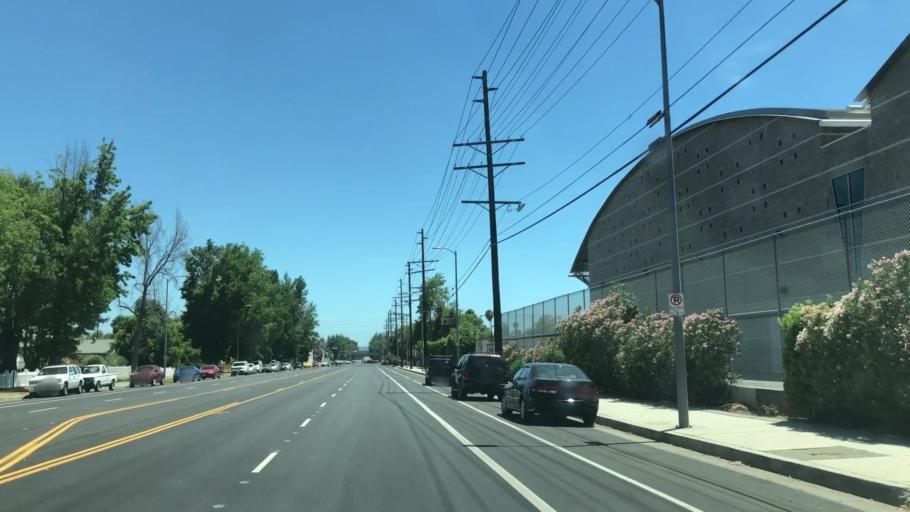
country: US
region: California
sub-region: Los Angeles County
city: San Fernando
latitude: 34.2752
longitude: -118.4848
